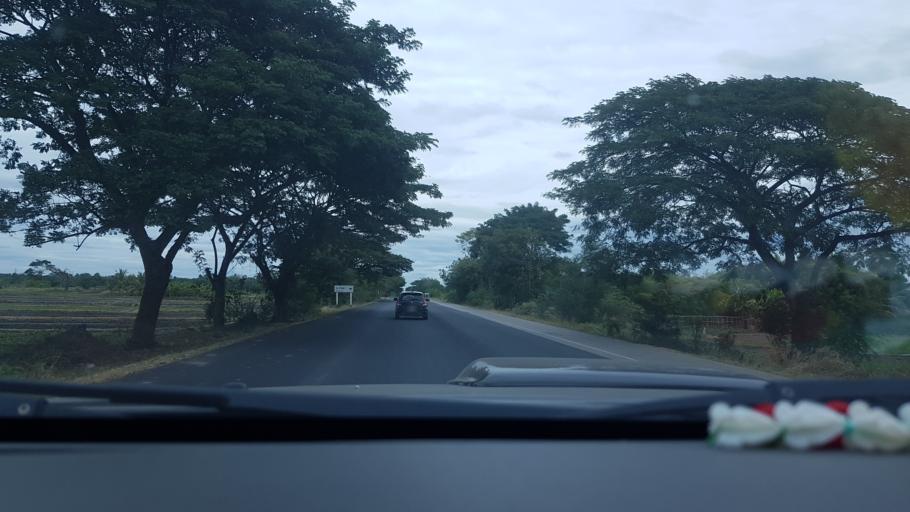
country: TH
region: Phetchabun
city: Phetchabun
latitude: 16.4586
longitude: 101.1191
